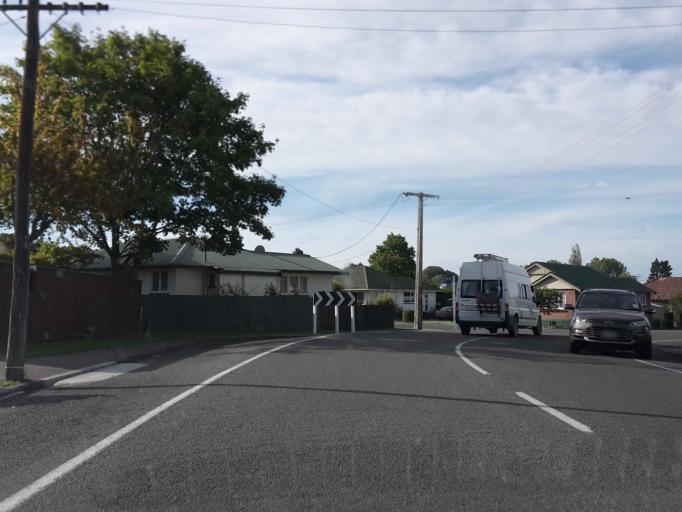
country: NZ
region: Canterbury
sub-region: Timaru District
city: Pleasant Point
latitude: -44.0944
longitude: 171.2405
